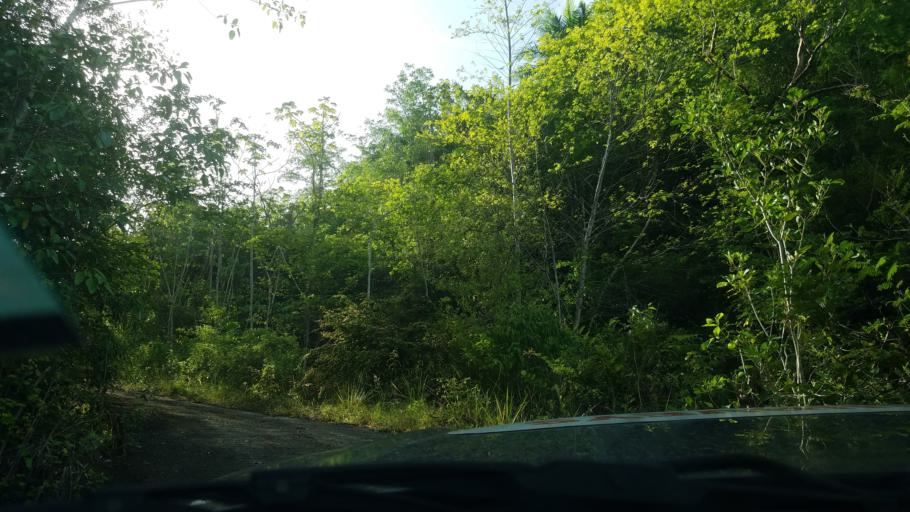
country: LC
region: Anse-la-Raye
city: Anse La Raye
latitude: 13.9512
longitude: -61.0392
